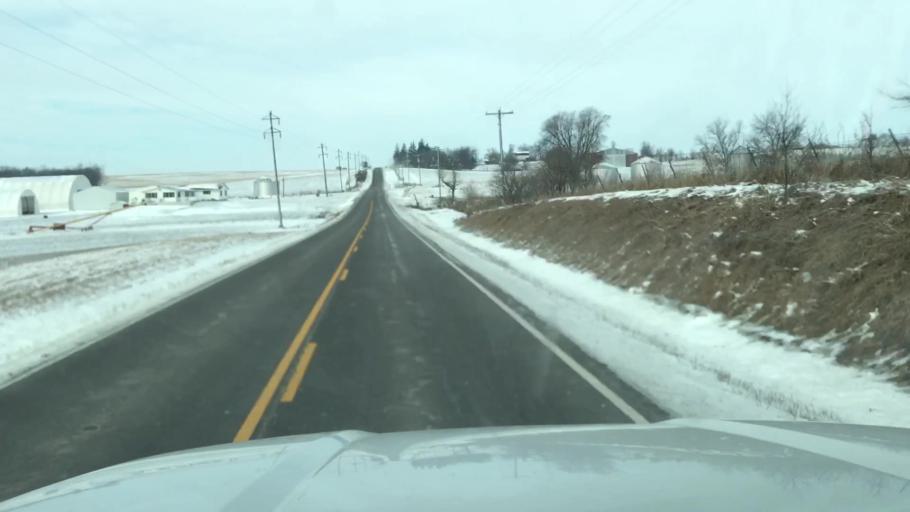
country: US
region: Missouri
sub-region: Holt County
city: Mound City
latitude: 40.1301
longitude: -95.1225
